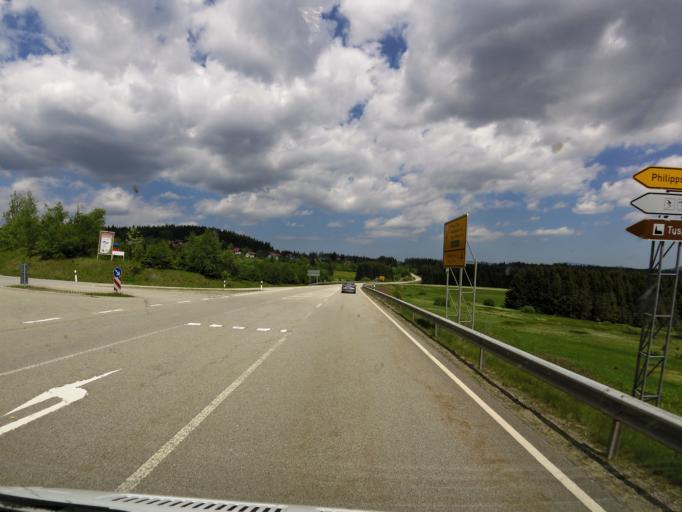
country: DE
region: Bavaria
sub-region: Lower Bavaria
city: Philippsreut
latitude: 48.8619
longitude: 13.6789
